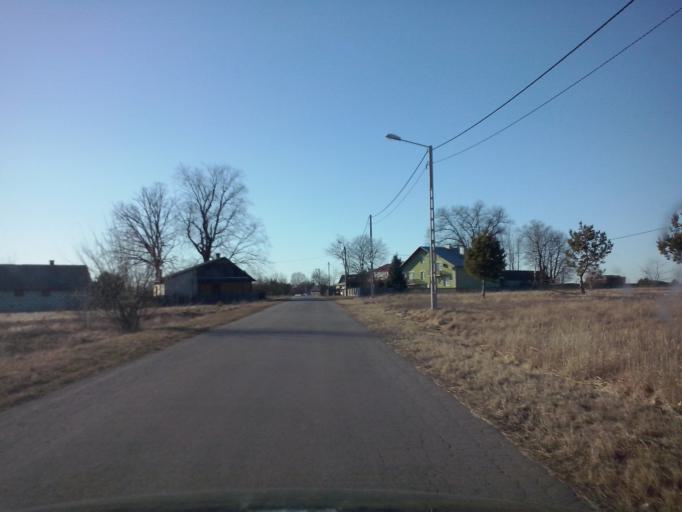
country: PL
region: Subcarpathian Voivodeship
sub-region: Powiat nizanski
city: Harasiuki
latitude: 50.5347
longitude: 22.4739
